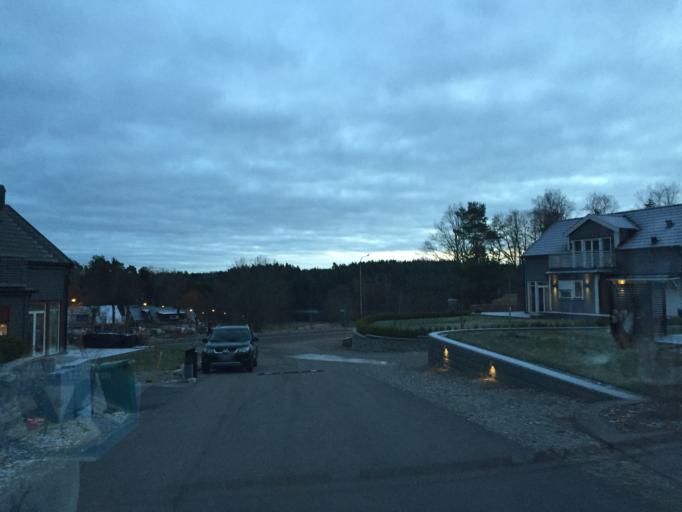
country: SE
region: Stockholm
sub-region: Salems Kommun
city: Ronninge
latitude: 59.1849
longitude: 17.7292
